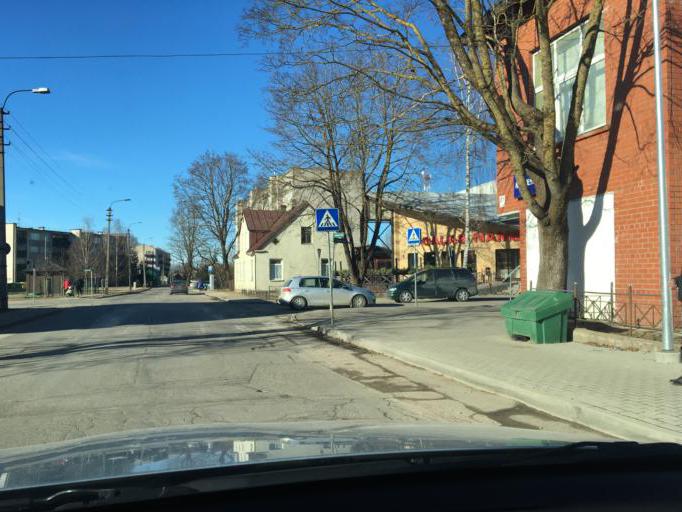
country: LV
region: Jekabpils Rajons
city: Jekabpils
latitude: 56.4900
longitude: 25.8652
